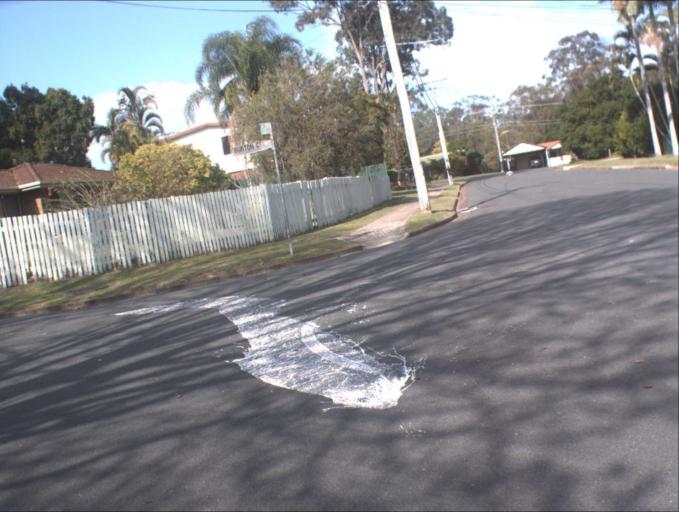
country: AU
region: Queensland
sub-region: Logan
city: Park Ridge South
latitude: -27.6876
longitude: 153.0189
